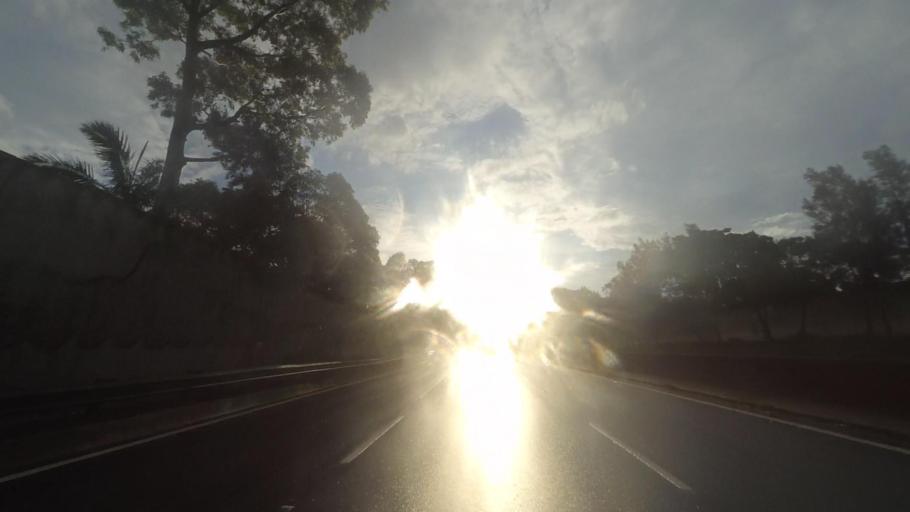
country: AU
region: New South Wales
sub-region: Wollongong
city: Mount Ousley
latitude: -34.4016
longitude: 150.8757
